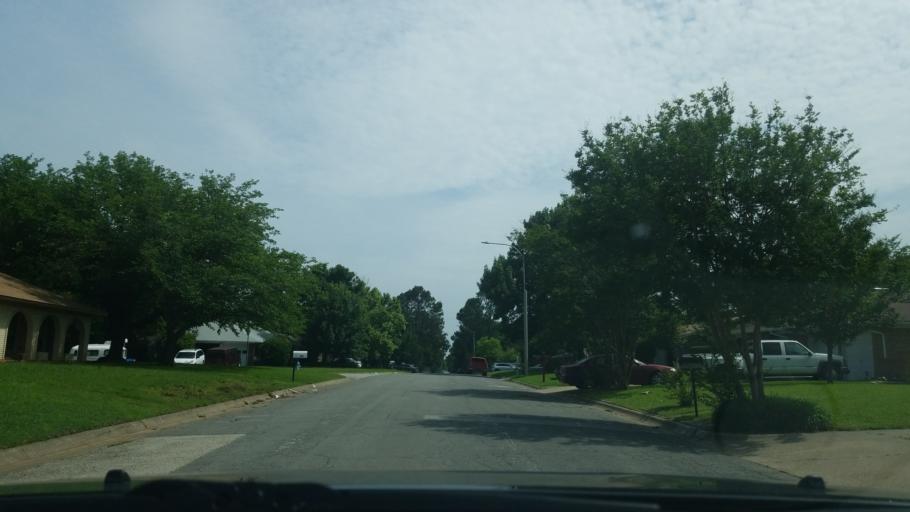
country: US
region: Texas
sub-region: Denton County
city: Denton
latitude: 33.2358
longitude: -97.1514
